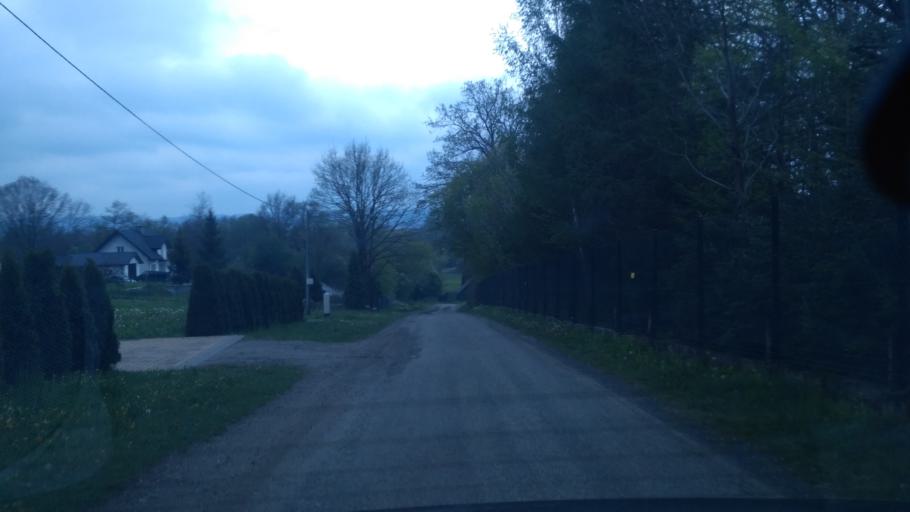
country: PL
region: Subcarpathian Voivodeship
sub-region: Powiat sanocki
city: Sanok
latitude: 49.5725
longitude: 22.2206
